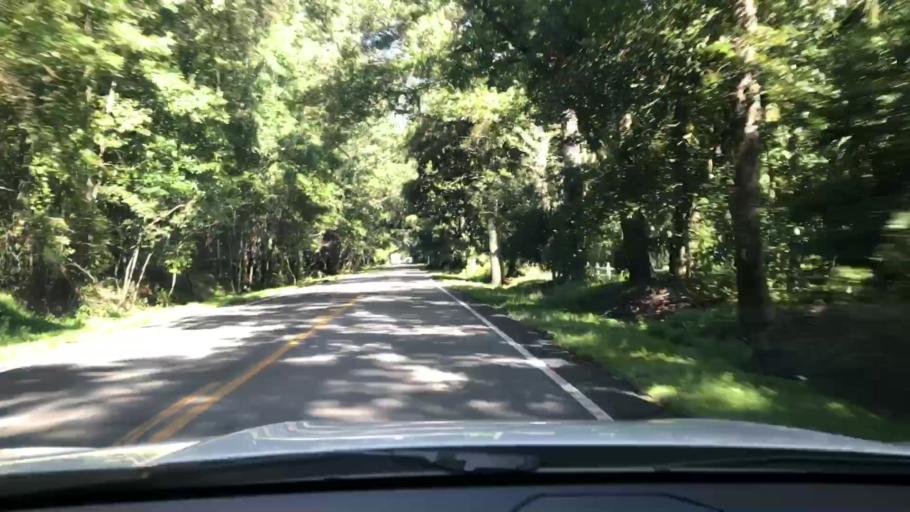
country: US
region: South Carolina
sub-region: Berkeley County
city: Hanahan
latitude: 32.8702
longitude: -80.0892
